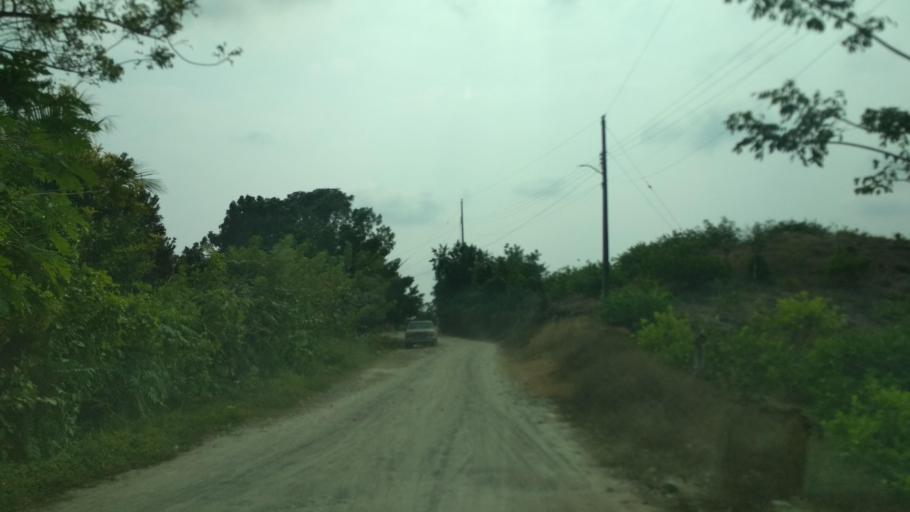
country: MM
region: Kayah
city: Loikaw
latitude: 20.2145
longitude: 97.2848
